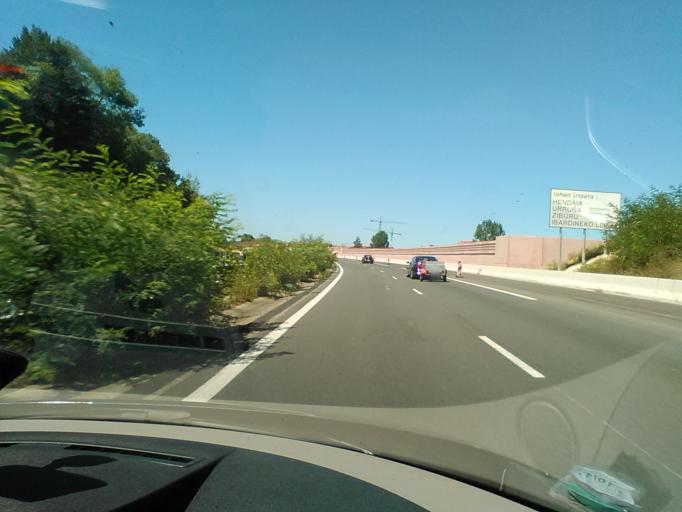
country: FR
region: Aquitaine
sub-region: Departement des Pyrenees-Atlantiques
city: Ciboure
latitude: 43.3750
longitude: -1.6651
